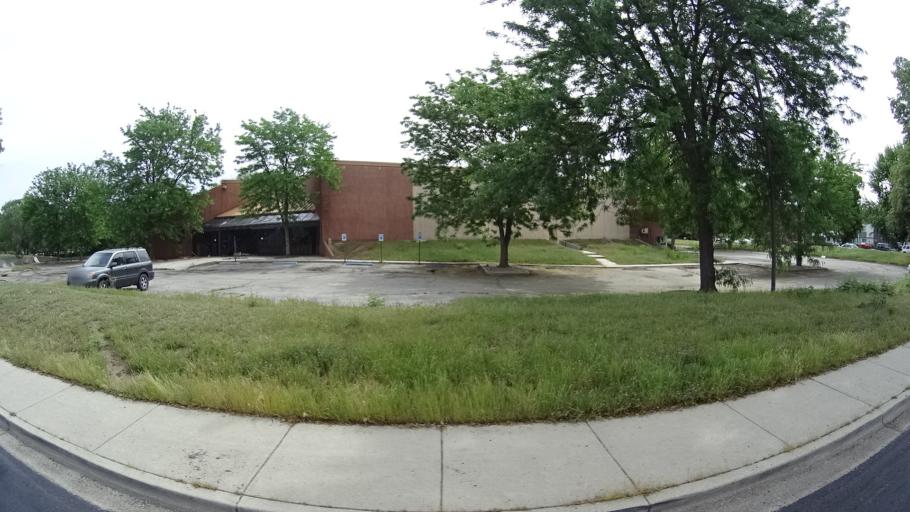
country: US
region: Idaho
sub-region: Ada County
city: Boise
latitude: 43.5976
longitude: -116.1885
